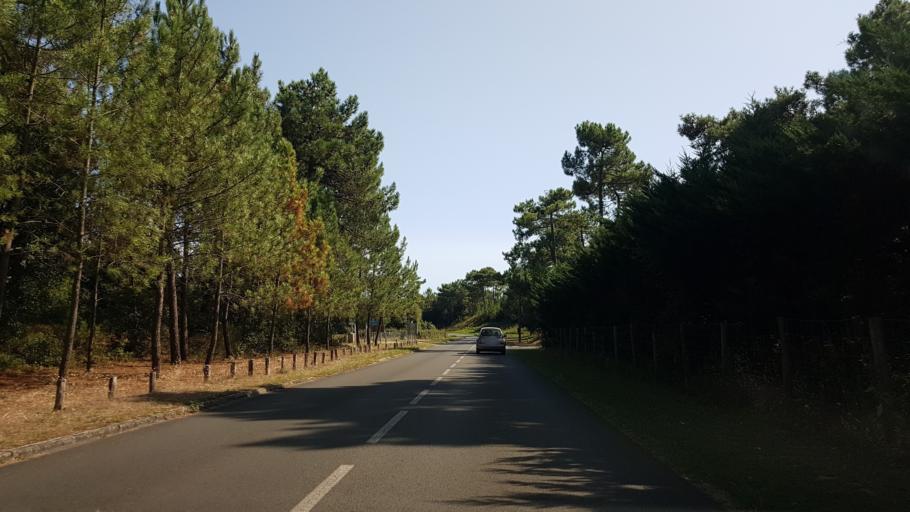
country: FR
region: Poitou-Charentes
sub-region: Departement de la Charente-Maritime
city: Les Mathes
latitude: 45.6970
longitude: -1.1959
